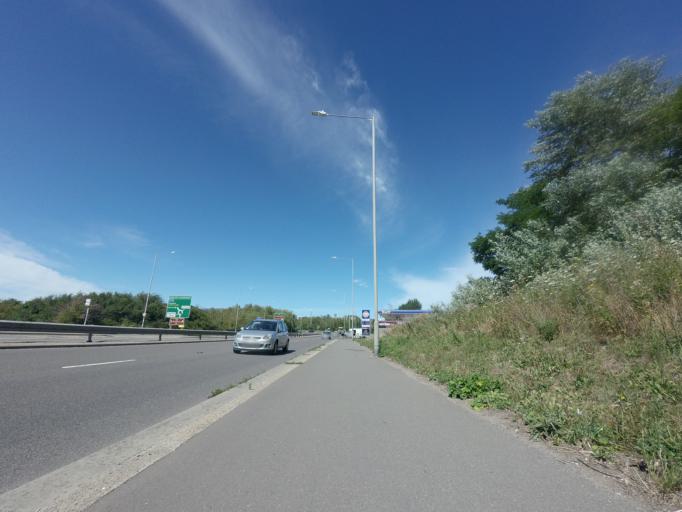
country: GB
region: England
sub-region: Kent
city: Sandwich
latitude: 51.3103
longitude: 1.3494
